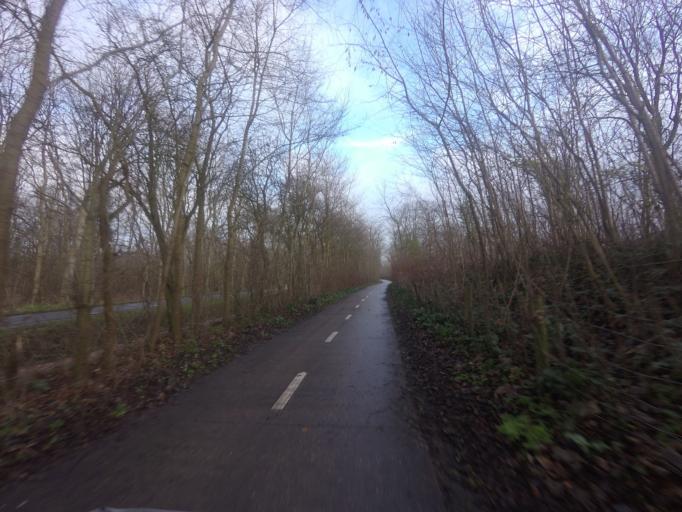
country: NL
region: North Holland
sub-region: Gemeente Texel
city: Den Burg
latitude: 53.1564
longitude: 4.8552
